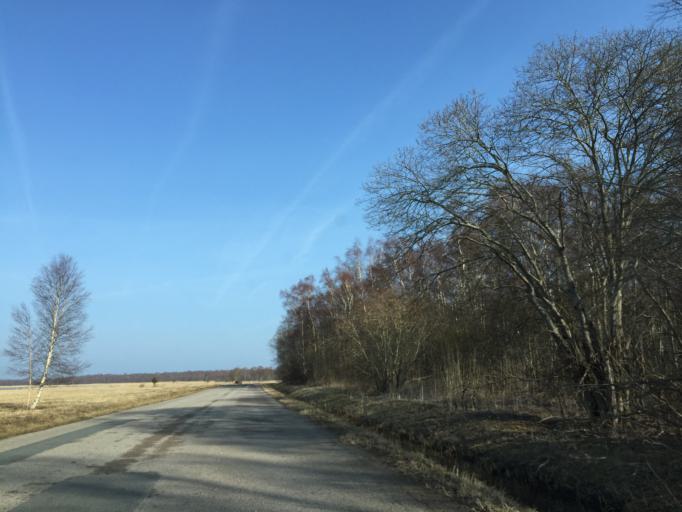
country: EE
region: Saare
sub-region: Kuressaare linn
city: Kuressaare
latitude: 58.0623
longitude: 22.1470
